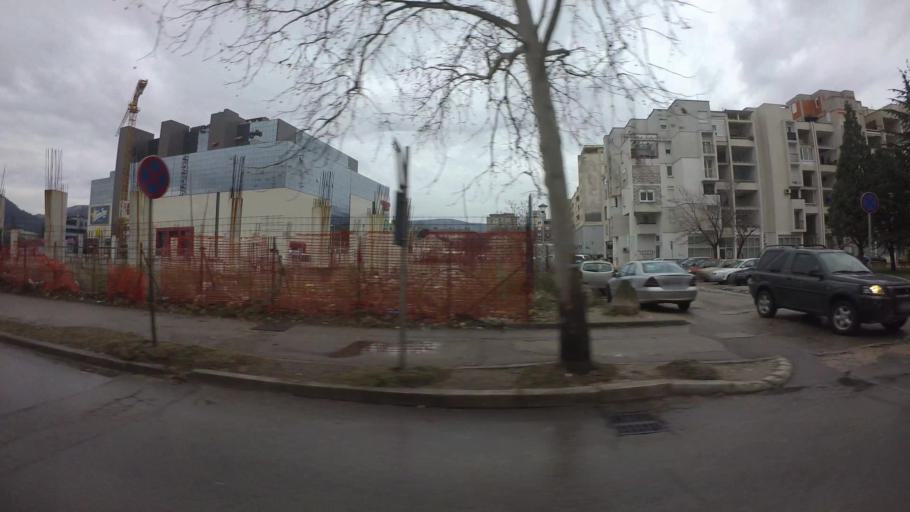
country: BA
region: Federation of Bosnia and Herzegovina
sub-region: Hercegovacko-Bosanski Kanton
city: Mostar
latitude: 43.3496
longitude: 17.8064
